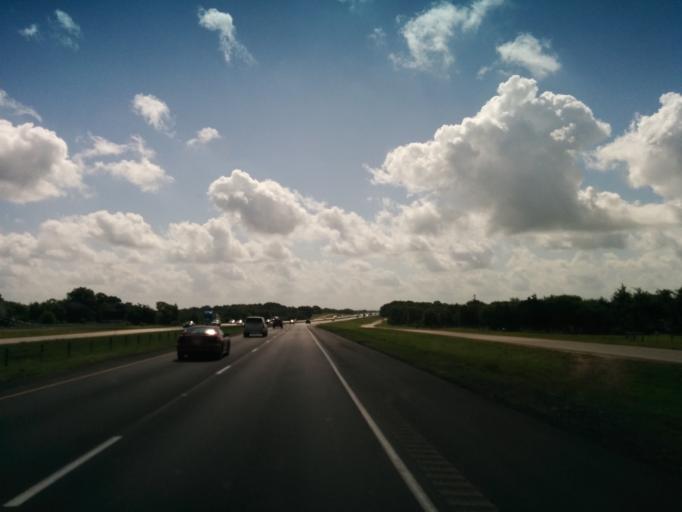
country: US
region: Texas
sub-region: Colorado County
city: Weimar
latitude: 29.6922
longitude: -96.7353
